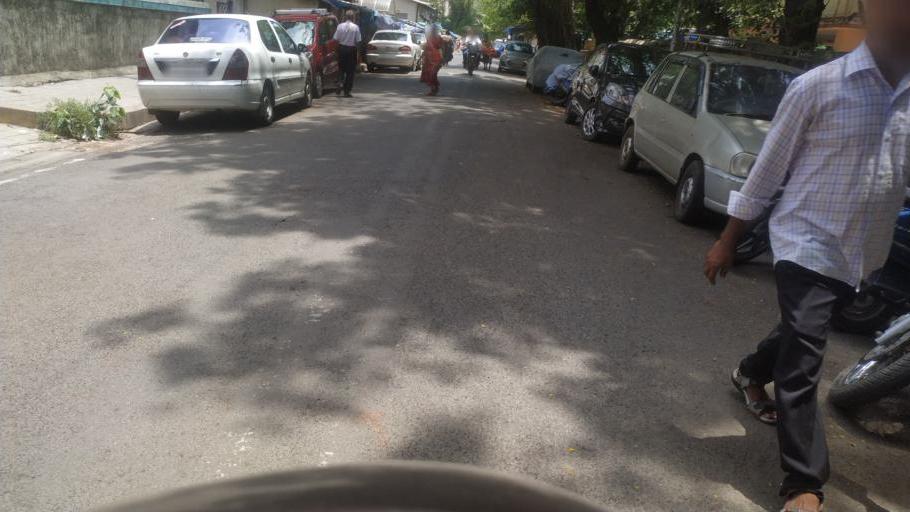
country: IN
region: Maharashtra
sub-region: Mumbai Suburban
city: Mumbai
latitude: 19.0158
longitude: 72.8254
